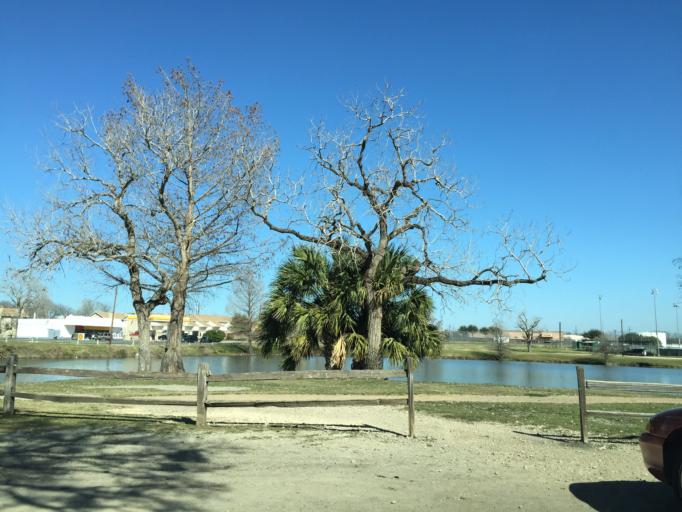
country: US
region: Texas
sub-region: Williamson County
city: Taylor
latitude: 30.5815
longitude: -97.4147
